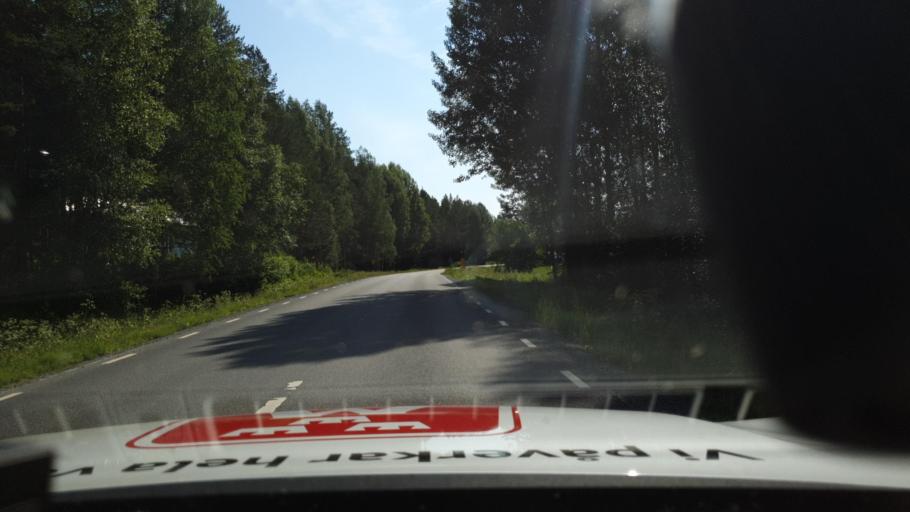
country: SE
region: Norrbotten
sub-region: Lulea Kommun
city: Sodra Sunderbyn
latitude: 65.8314
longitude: 21.9613
